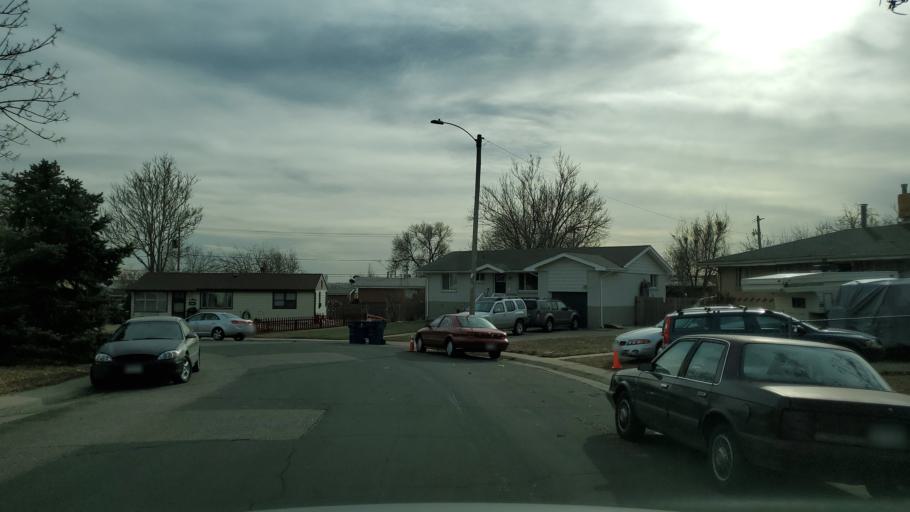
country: US
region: Colorado
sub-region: Adams County
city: Westminster
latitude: 39.8292
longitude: -105.0234
